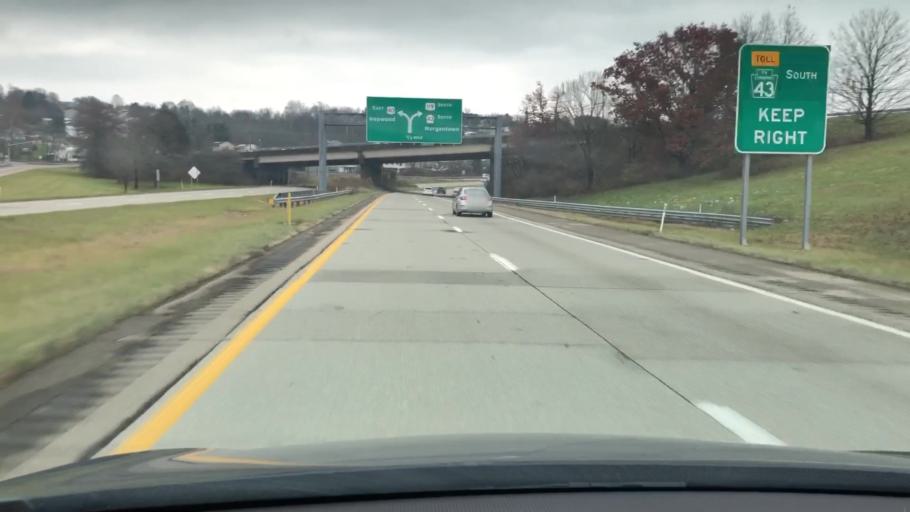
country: US
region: Pennsylvania
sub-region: Fayette County
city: South Uniontown
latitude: 39.8830
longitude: -79.7464
